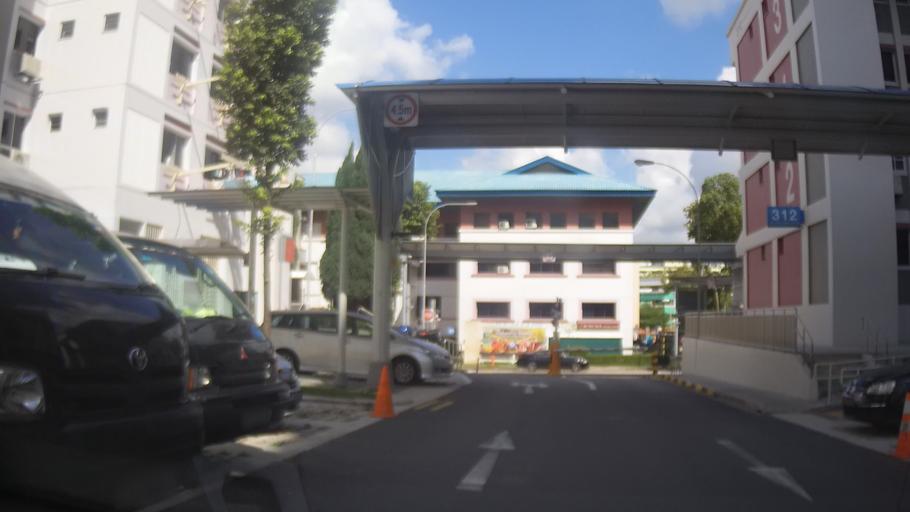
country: MY
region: Johor
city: Johor Bahru
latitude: 1.4303
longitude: 103.7760
